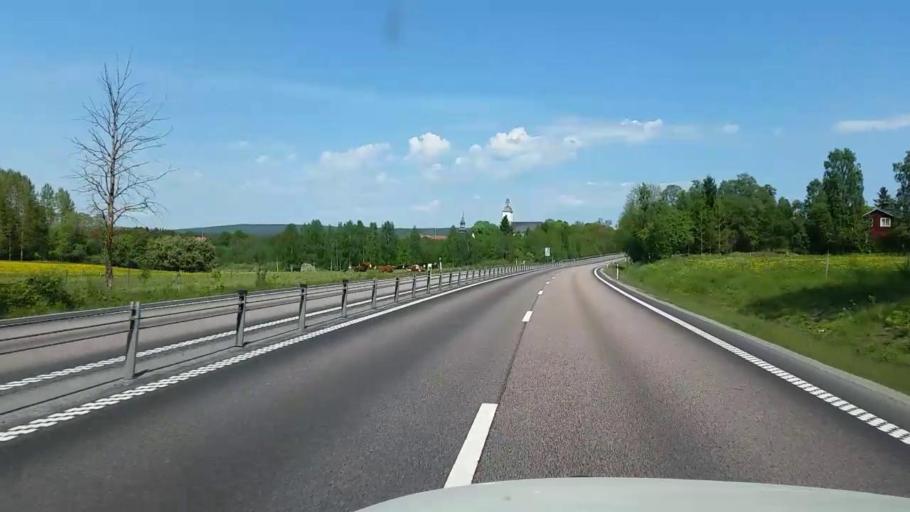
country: SE
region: Gaevleborg
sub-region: Hudiksvalls Kommun
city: Hudiksvall
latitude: 61.7488
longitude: 17.0791
